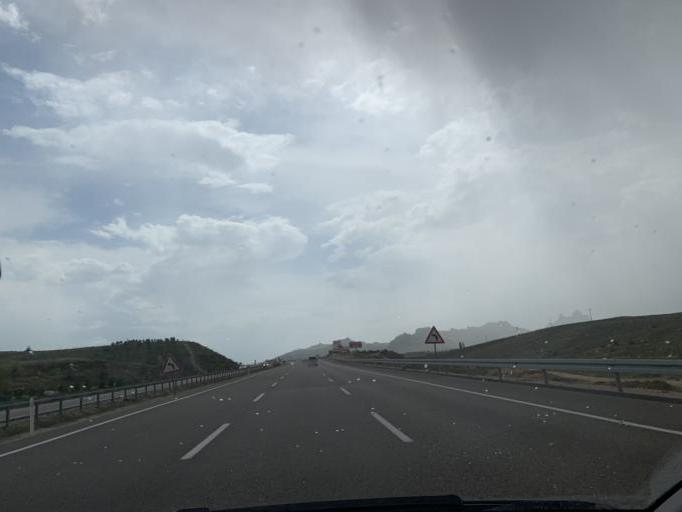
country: TR
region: Eskisehir
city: Sivrihisar
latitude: 39.4682
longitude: 31.5840
